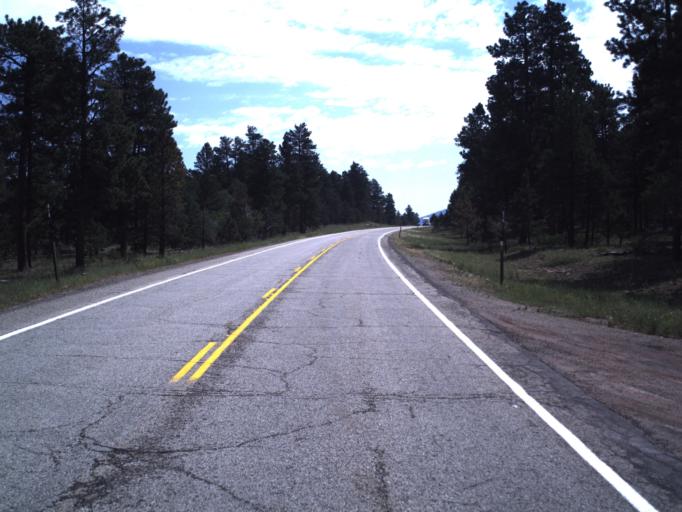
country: US
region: Utah
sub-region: Daggett County
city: Manila
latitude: 40.8525
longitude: -109.6066
